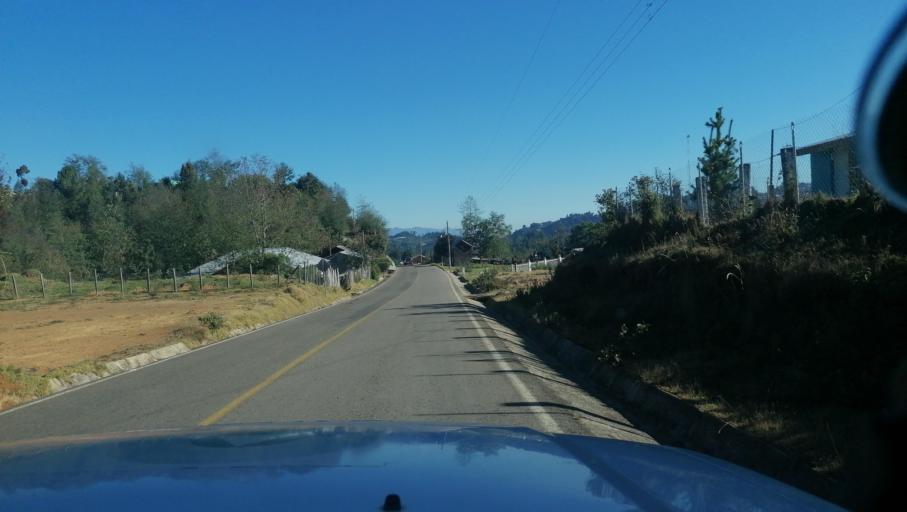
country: MX
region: Chiapas
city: Motozintla de Mendoza
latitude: 15.2404
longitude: -92.2305
